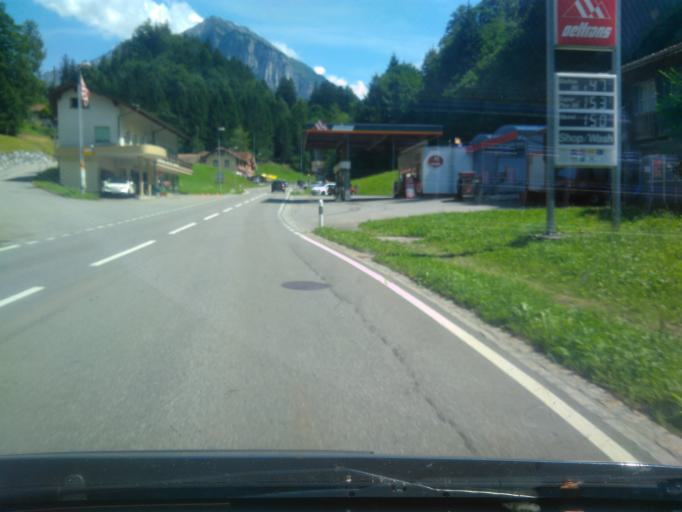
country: CH
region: Bern
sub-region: Interlaken-Oberhasli District
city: Meiringen
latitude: 46.7152
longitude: 8.2096
